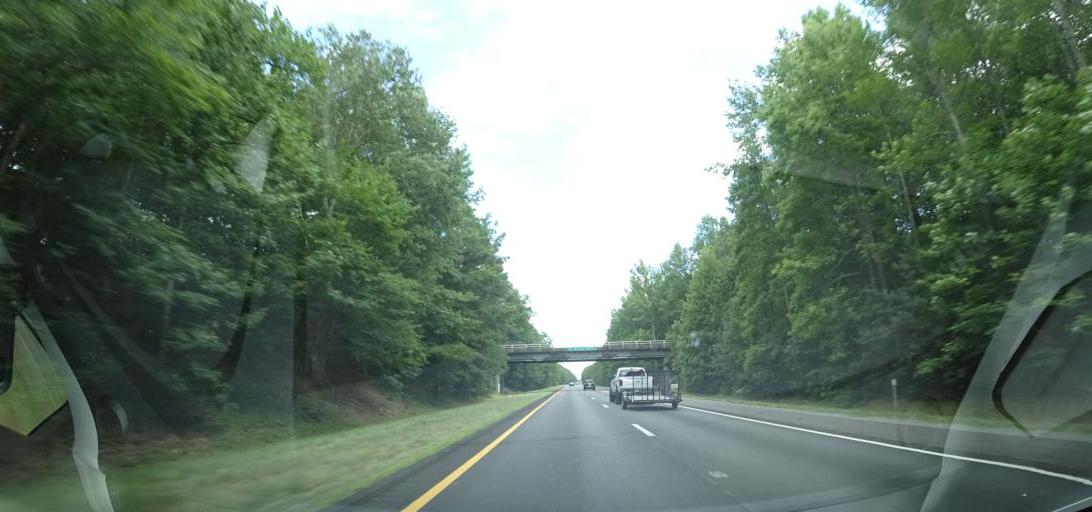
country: US
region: Virginia
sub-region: King William County
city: West Point
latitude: 37.4486
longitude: -76.8655
